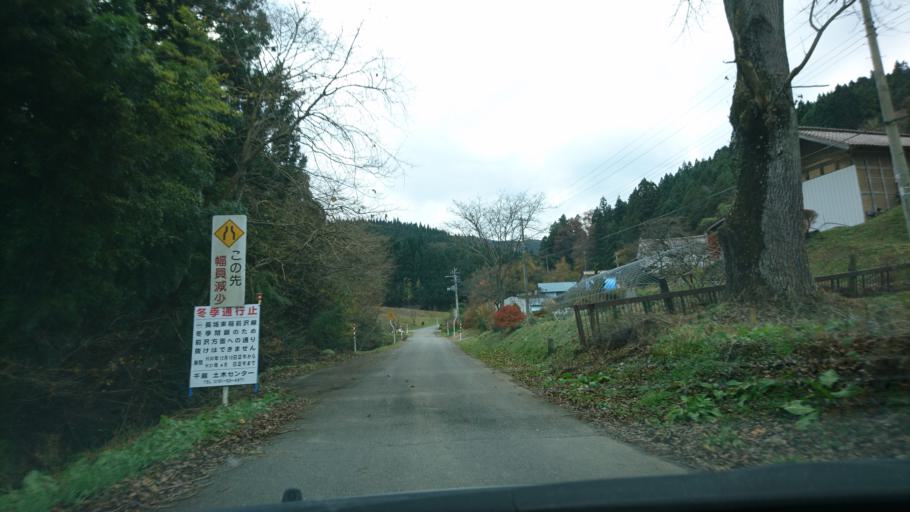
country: JP
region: Iwate
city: Ichinoseki
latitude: 39.0067
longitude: 141.2142
